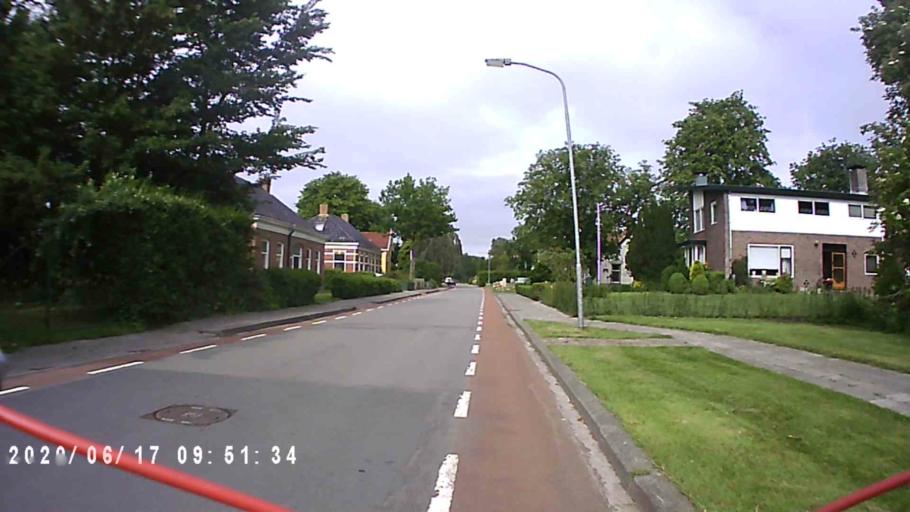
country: NL
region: Groningen
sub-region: Gemeente De Marne
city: Ulrum
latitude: 53.3597
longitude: 6.3284
